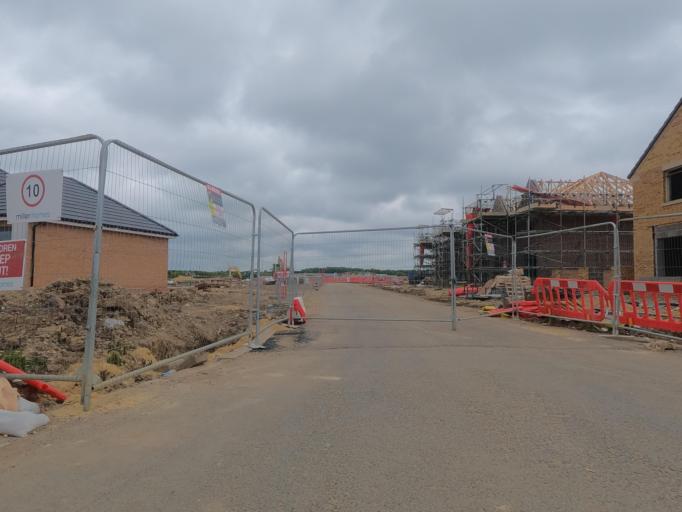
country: GB
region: England
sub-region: Northumberland
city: Blyth
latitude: 55.1035
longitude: -1.5269
